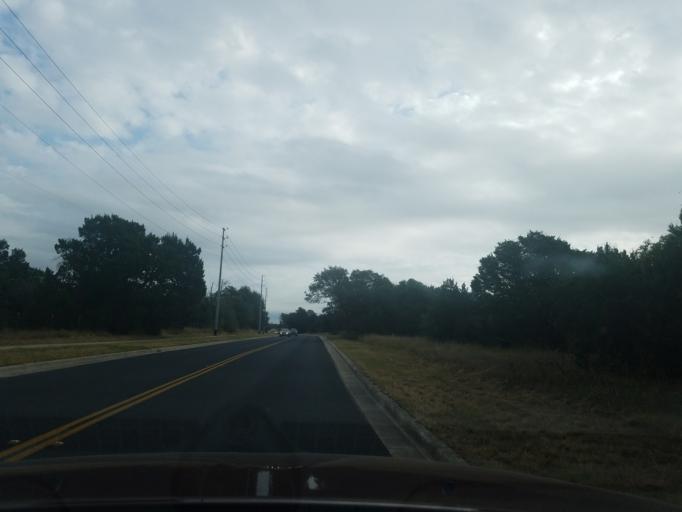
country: US
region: Texas
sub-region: Williamson County
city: Anderson Mill
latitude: 30.4841
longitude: -97.7837
